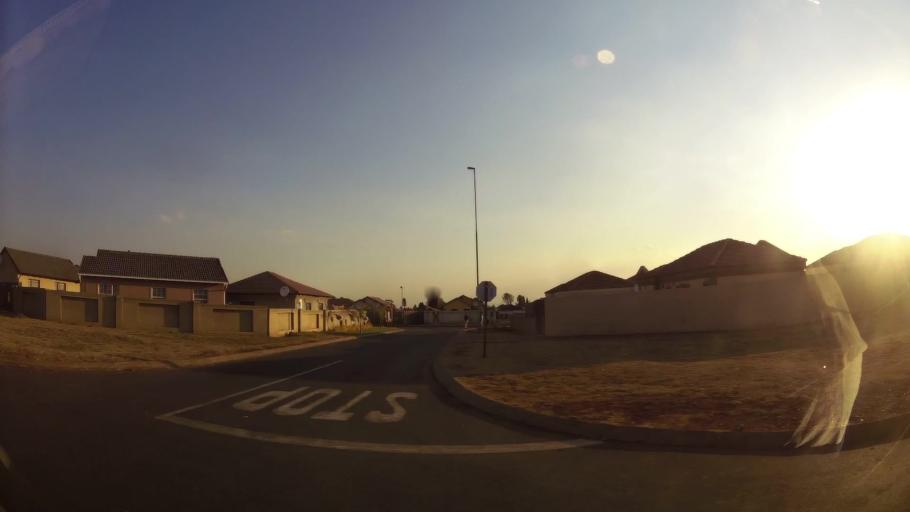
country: ZA
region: Gauteng
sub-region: Ekurhuleni Metropolitan Municipality
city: Boksburg
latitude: -26.3006
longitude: 28.2490
